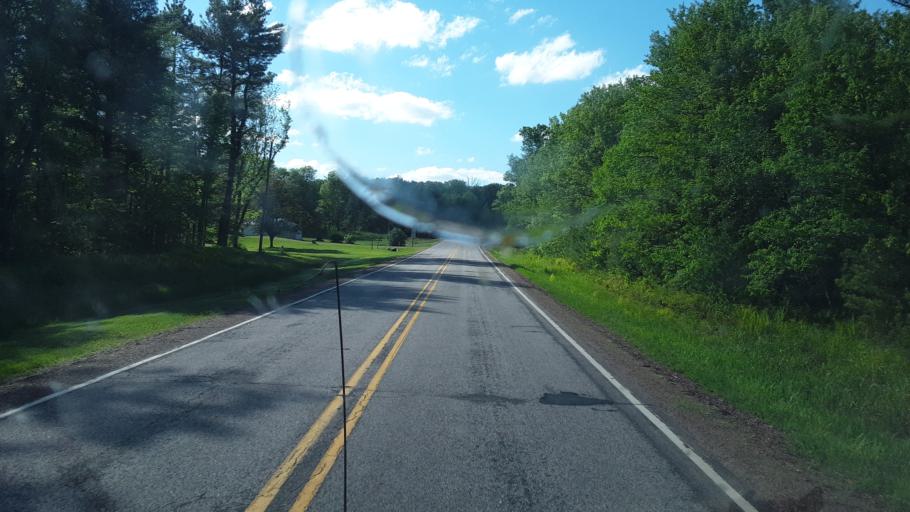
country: US
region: Wisconsin
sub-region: Wood County
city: Nekoosa
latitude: 44.3005
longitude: -90.1247
